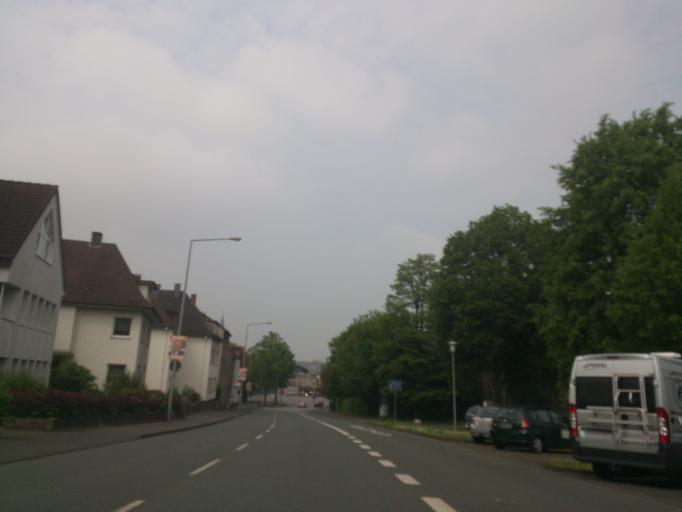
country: DE
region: North Rhine-Westphalia
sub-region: Regierungsbezirk Detmold
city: Paderborn
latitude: 51.7135
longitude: 8.7594
